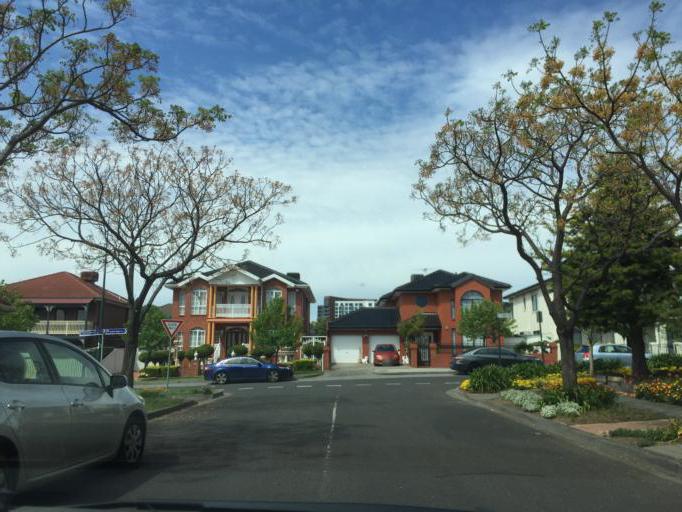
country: AU
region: Victoria
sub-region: Maribyrnong
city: Maidstone
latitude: -37.7740
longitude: 144.8759
